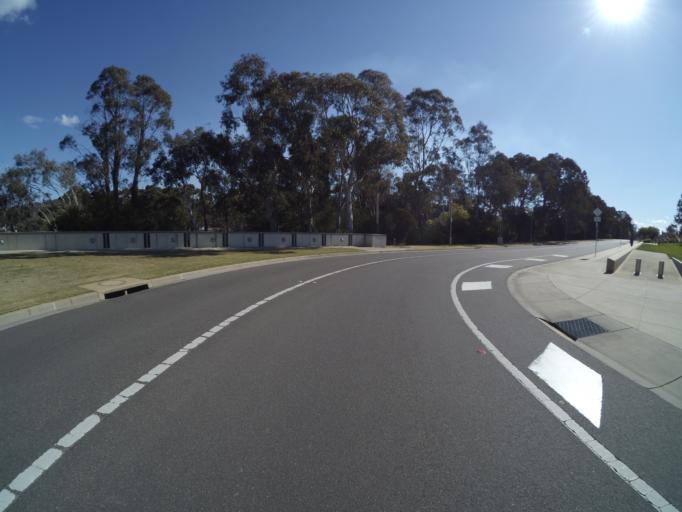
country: AU
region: Australian Capital Territory
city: Forrest
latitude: -35.3107
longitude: 149.1247
